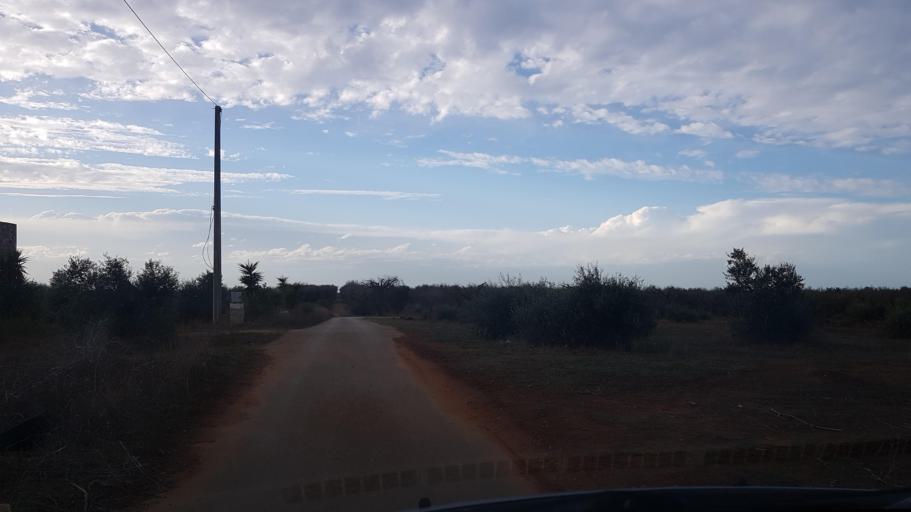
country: IT
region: Apulia
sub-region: Provincia di Brindisi
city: Torchiarolo
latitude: 40.4980
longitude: 18.0827
